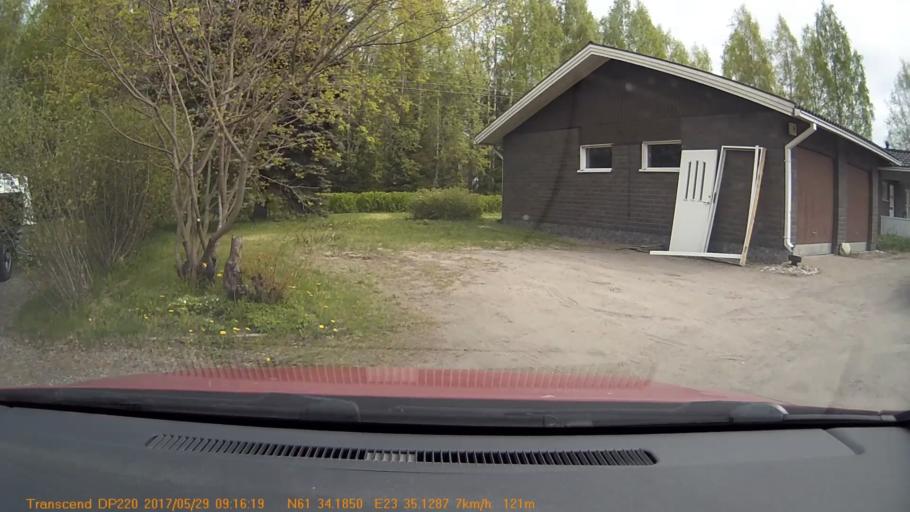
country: FI
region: Pirkanmaa
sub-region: Tampere
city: Yloejaervi
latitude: 61.5697
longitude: 23.5855
